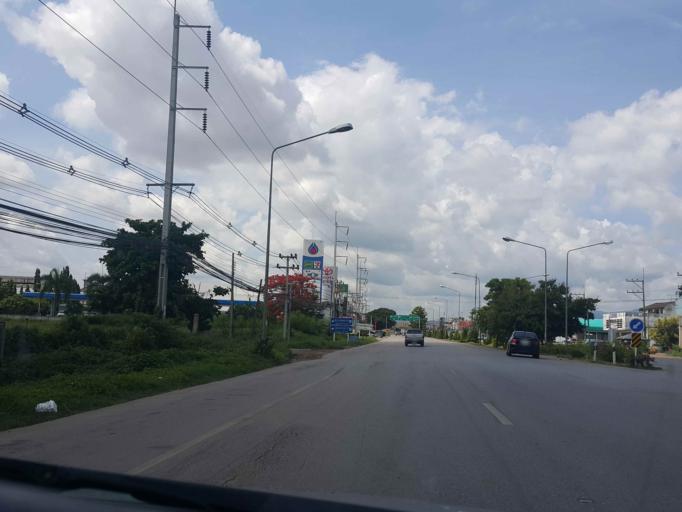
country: TH
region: Phayao
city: Phayao
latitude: 19.1469
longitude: 99.9120
